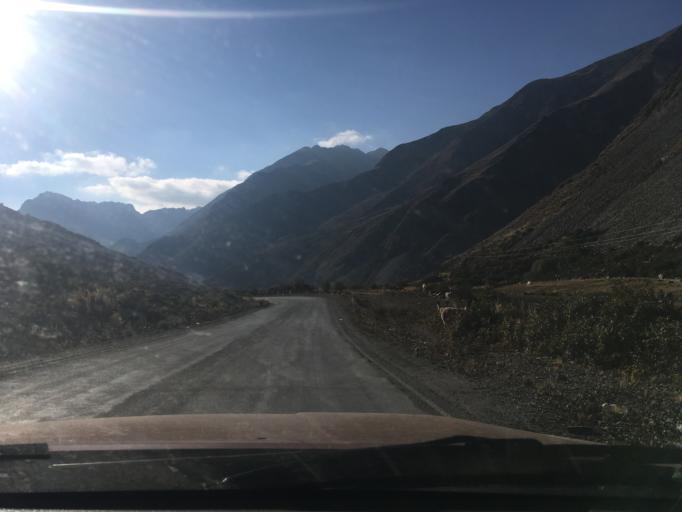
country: BO
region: La Paz
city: Quime
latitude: -17.0019
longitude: -67.2772
